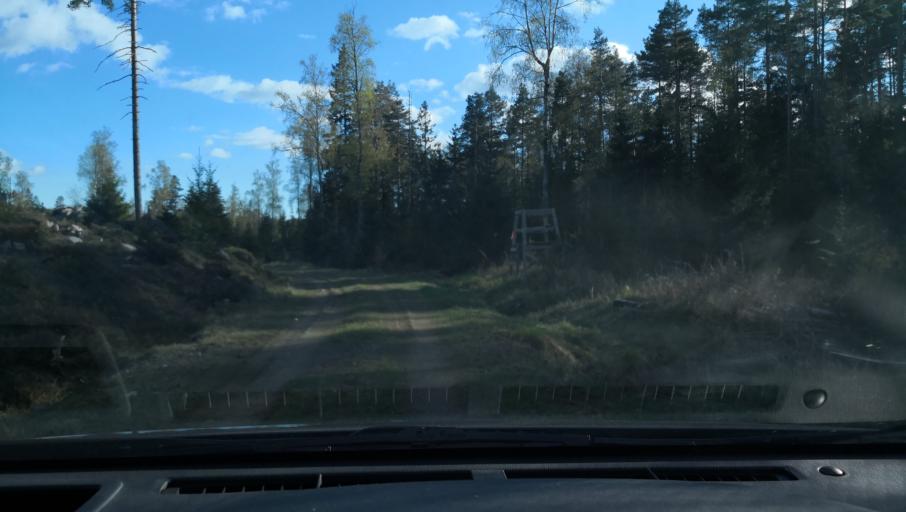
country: SE
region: OErebro
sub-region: Askersunds Kommun
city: Asbro
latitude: 58.8728
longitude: 15.1248
